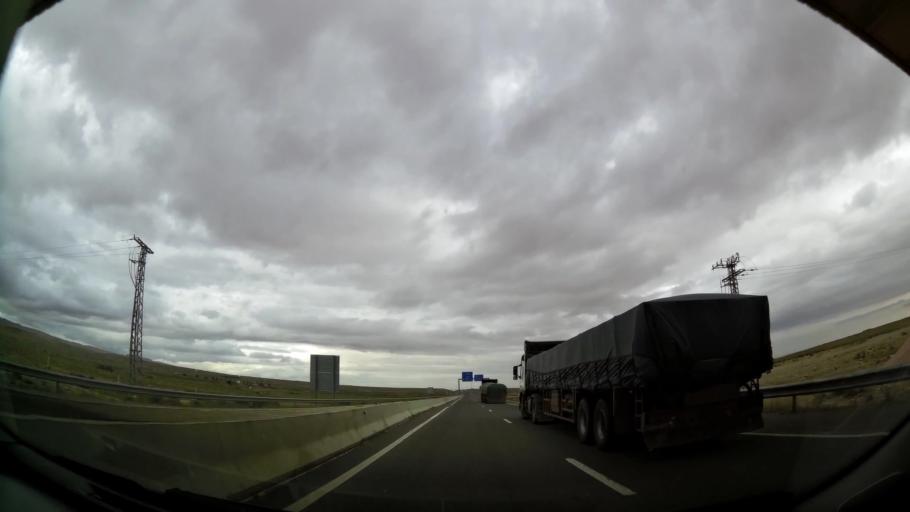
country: MA
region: Taza-Al Hoceima-Taounate
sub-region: Taza
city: Taza
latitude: 34.3093
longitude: -3.7325
